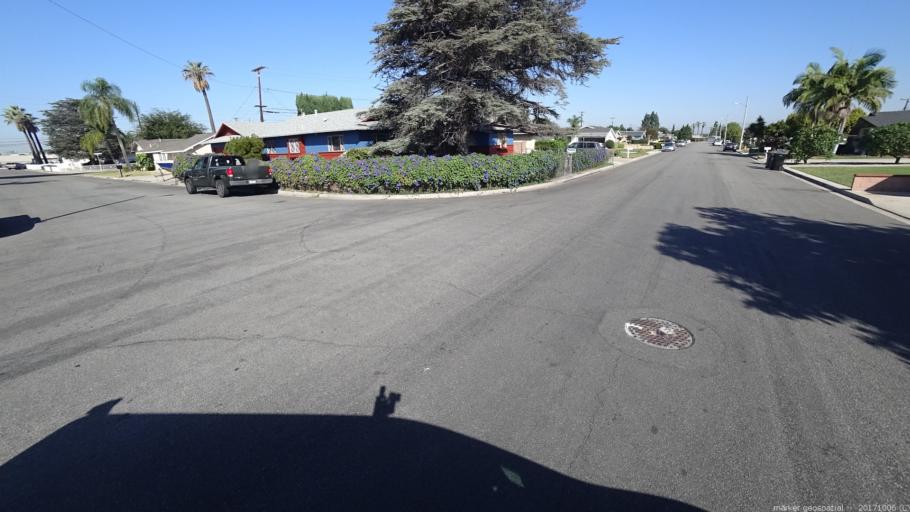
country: US
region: California
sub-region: Orange County
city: Stanton
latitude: 33.7820
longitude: -117.9822
